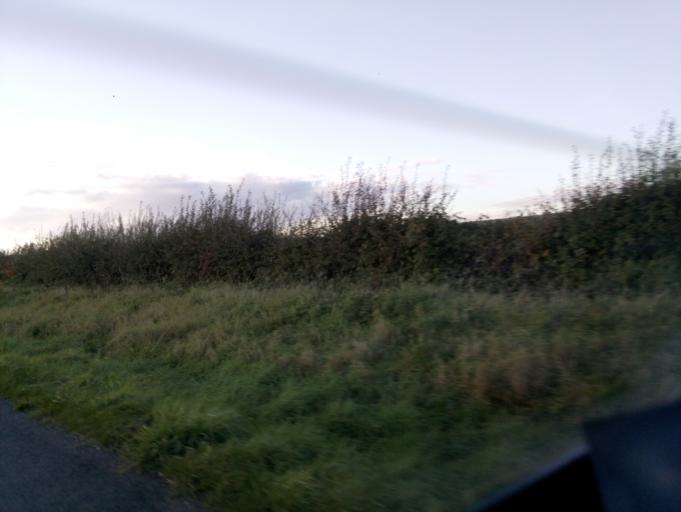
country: GB
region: England
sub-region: Worcestershire
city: Upton upon Severn
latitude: 52.0119
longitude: -2.2888
